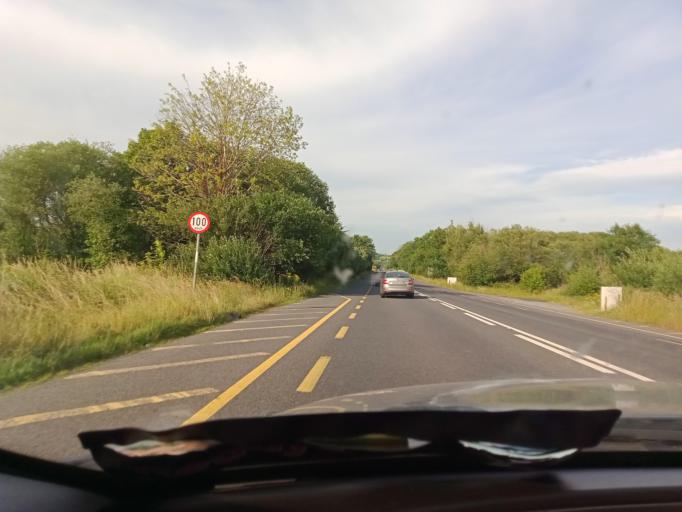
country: IE
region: Ulster
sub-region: An Cabhan
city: Cavan
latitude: 53.9414
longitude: -7.3886
